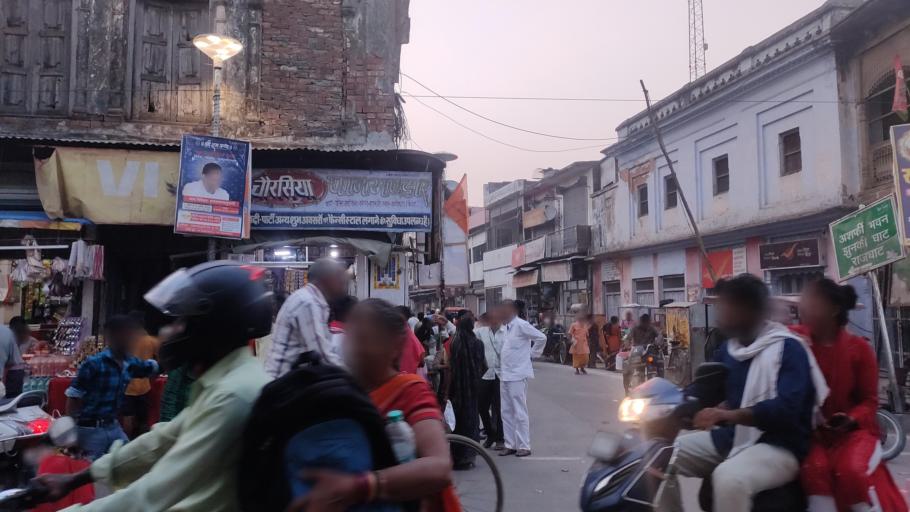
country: IN
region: Uttar Pradesh
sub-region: Faizabad
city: Ayodhya
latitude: 26.7993
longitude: 82.2045
